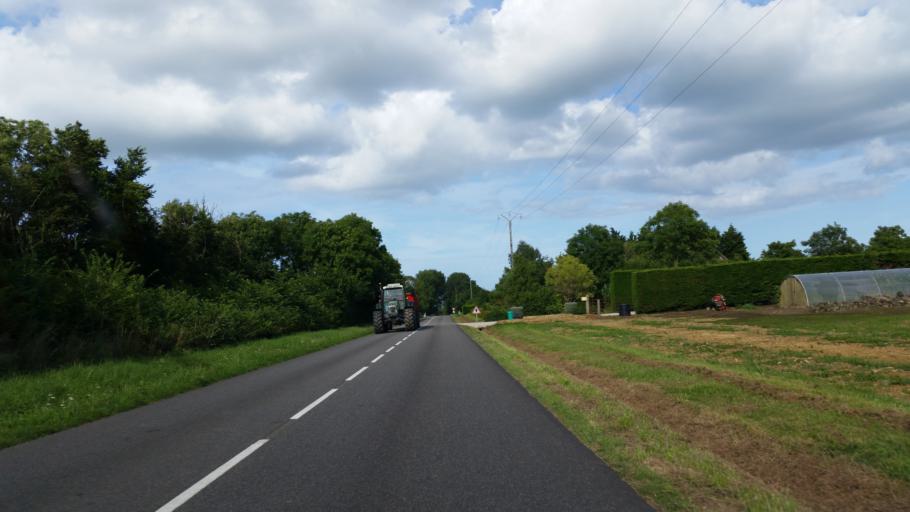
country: FR
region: Lower Normandy
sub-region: Departement de la Manche
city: Sainte-Mere-Eglise
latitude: 49.4520
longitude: -1.2724
